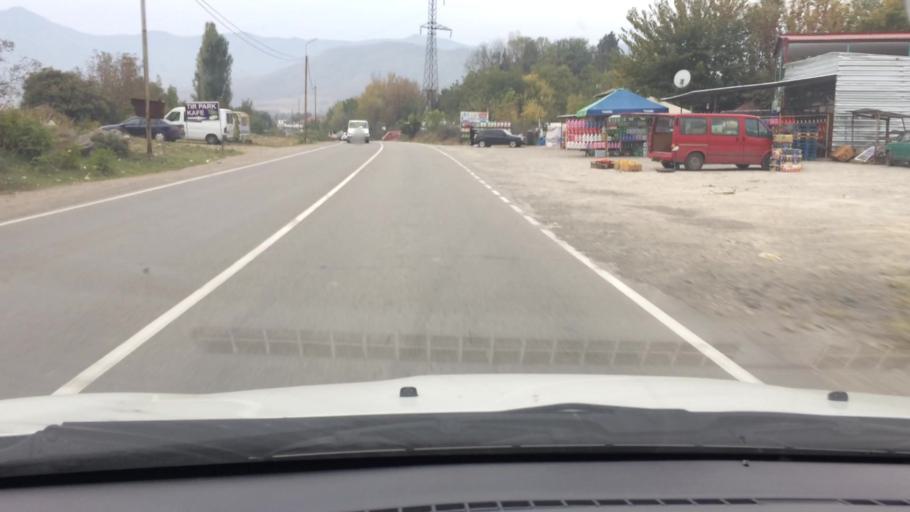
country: AM
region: Tavush
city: Bagratashen
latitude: 41.2535
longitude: 44.7997
